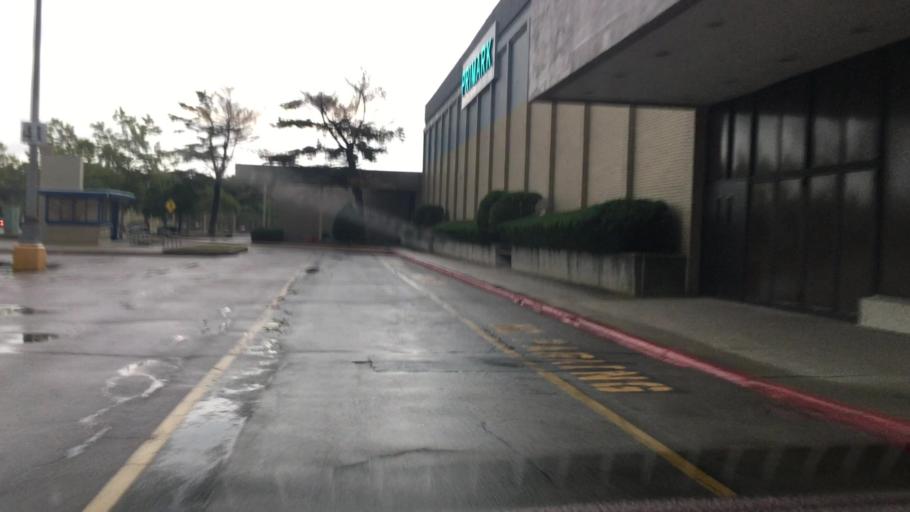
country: US
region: Massachusetts
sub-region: Middlesex County
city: Burlington
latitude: 42.4841
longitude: -71.2155
